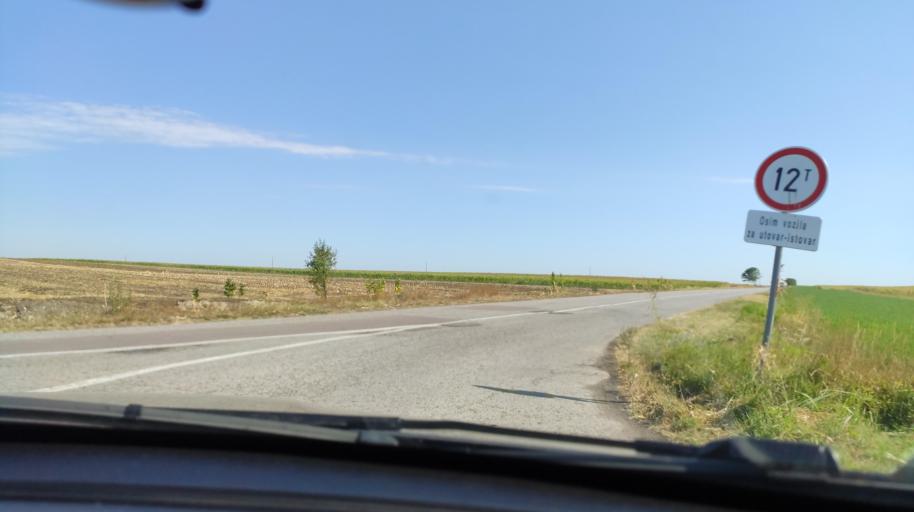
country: RS
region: Autonomna Pokrajina Vojvodina
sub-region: Severnobacki Okrug
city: Backa Topola
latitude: 45.8440
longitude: 19.5579
